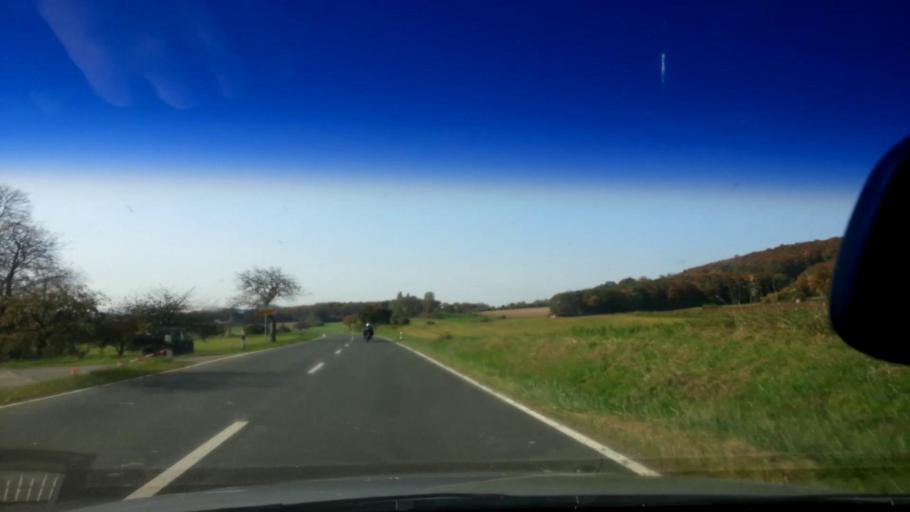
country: DE
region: Bavaria
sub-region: Upper Franconia
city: Schesslitz
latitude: 49.9808
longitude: 11.0811
